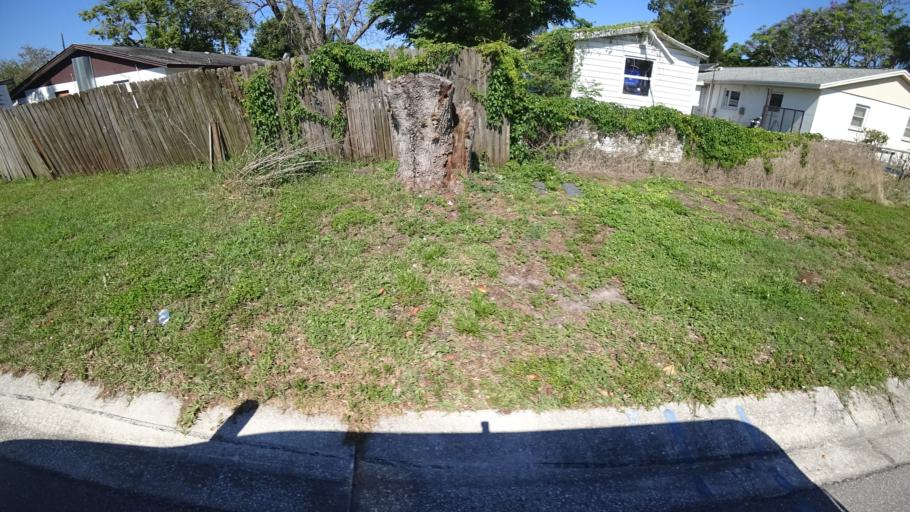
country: US
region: Florida
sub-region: Manatee County
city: South Bradenton
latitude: 27.4673
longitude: -82.5965
